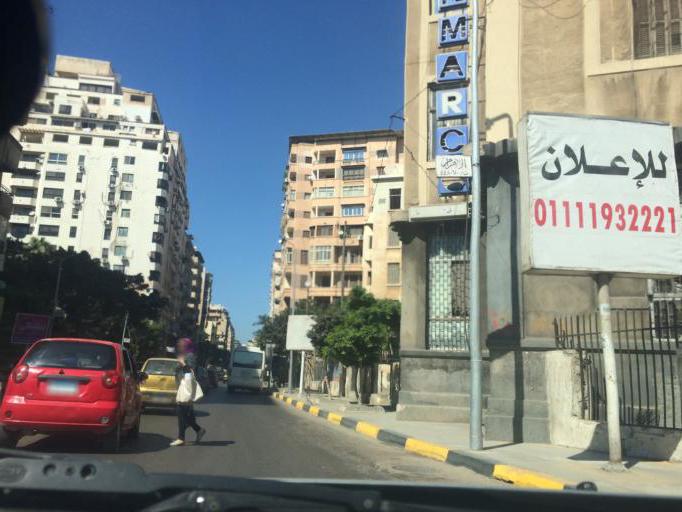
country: EG
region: Alexandria
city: Alexandria
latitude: 31.2329
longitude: 29.9574
